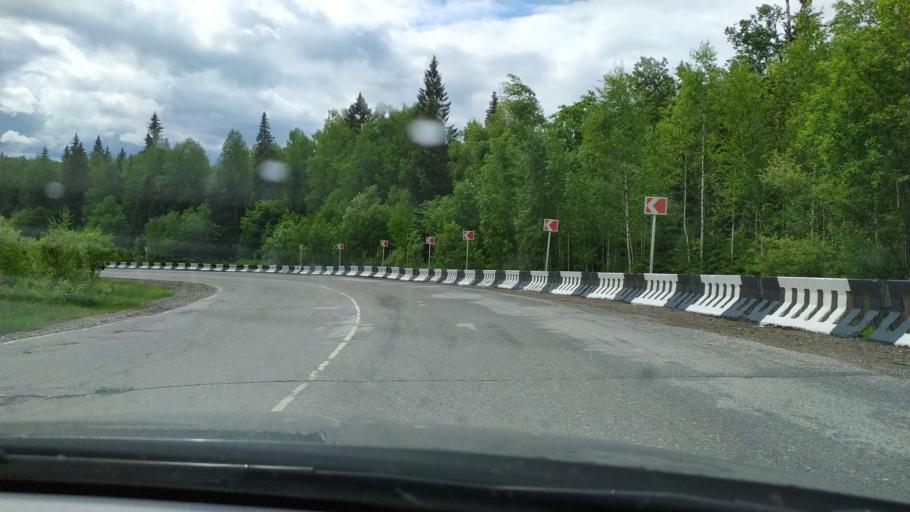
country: RU
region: Perm
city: Gremyachinsk
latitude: 58.4455
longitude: 57.8672
